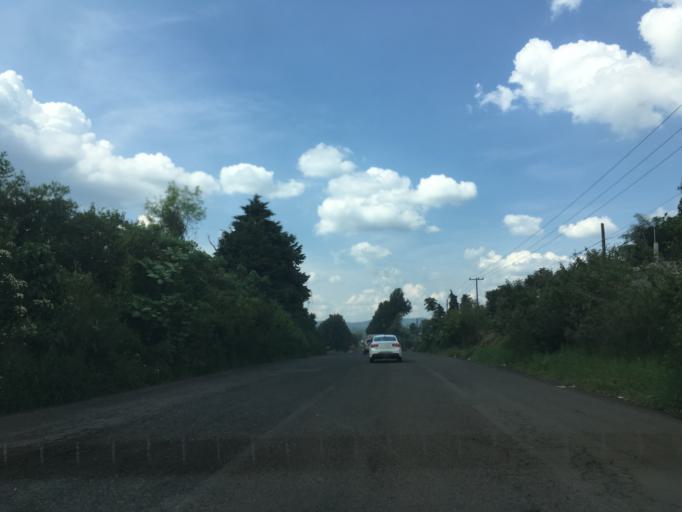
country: MX
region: Michoacan
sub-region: Tingueindin
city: Tingueindin
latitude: 19.7585
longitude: -102.4909
